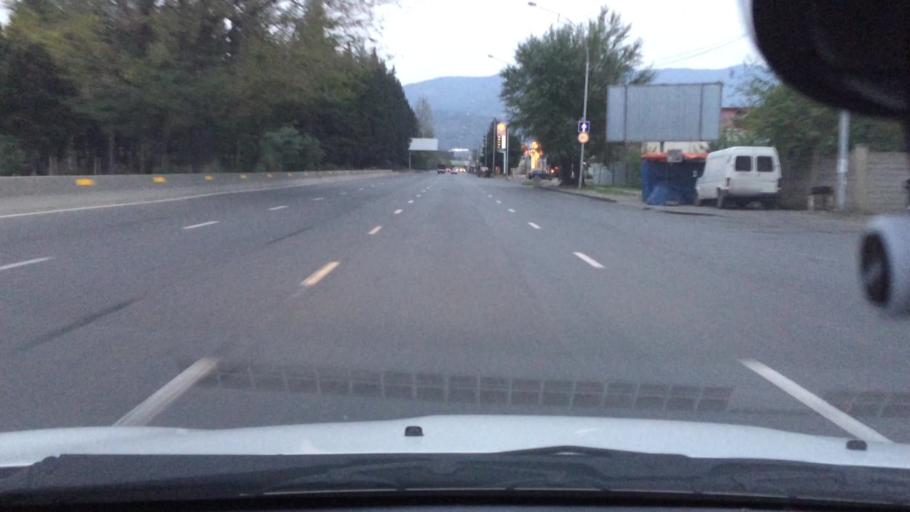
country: GE
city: Zahesi
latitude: 41.7992
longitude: 44.7710
